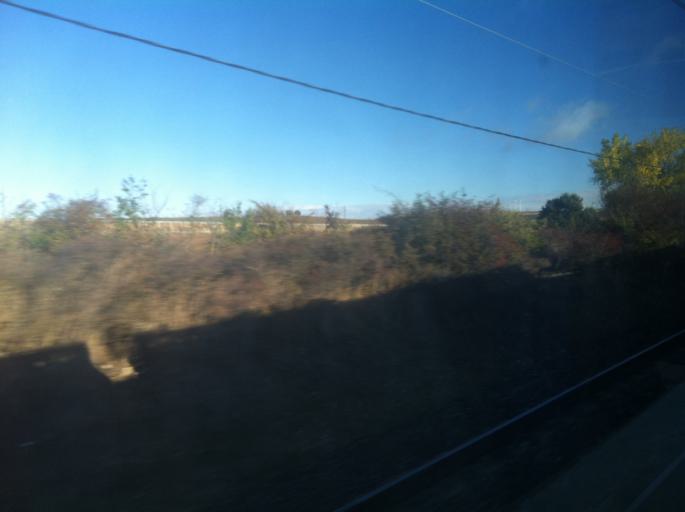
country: ES
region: Castille and Leon
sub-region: Provincia de Burgos
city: Villaverde-Mogina
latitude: 42.1666
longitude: -4.0720
